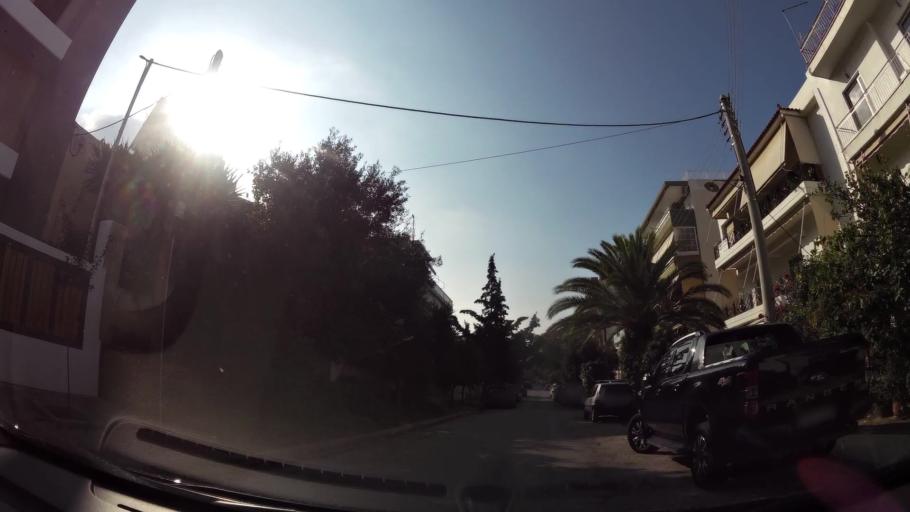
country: GR
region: Attica
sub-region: Nomarchia Athinas
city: Ilioupoli
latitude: 37.9318
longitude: 23.7619
